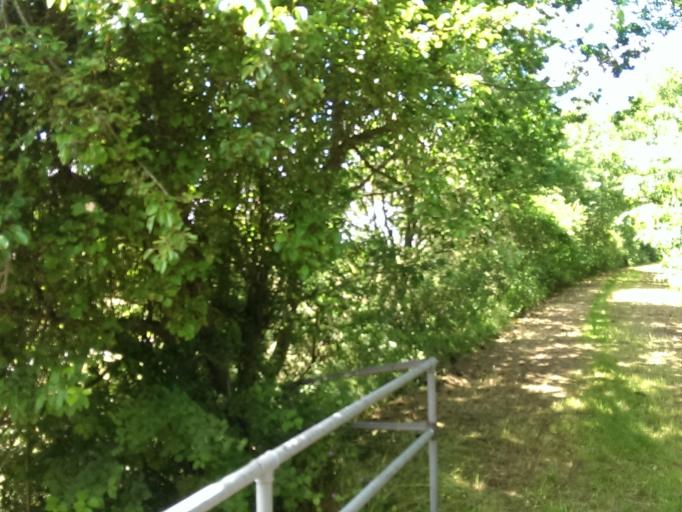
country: DK
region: Central Jutland
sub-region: Odder Kommune
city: Odder
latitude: 55.9257
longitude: 10.1030
